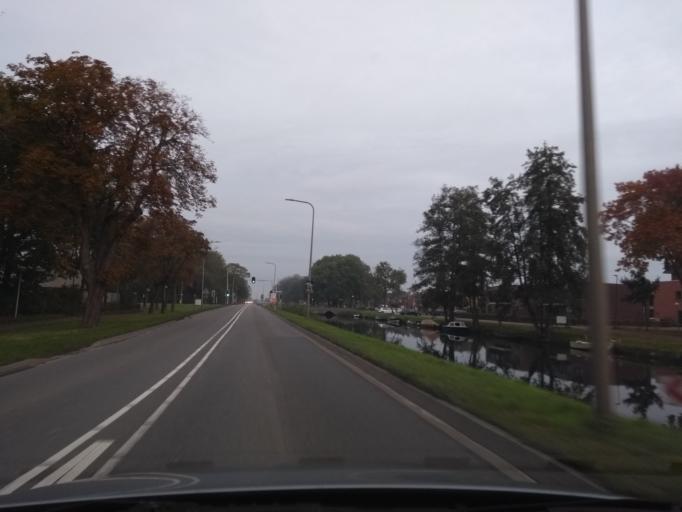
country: NL
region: Overijssel
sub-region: Gemeente Zwartewaterland
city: Hasselt
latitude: 52.5935
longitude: 6.0949
